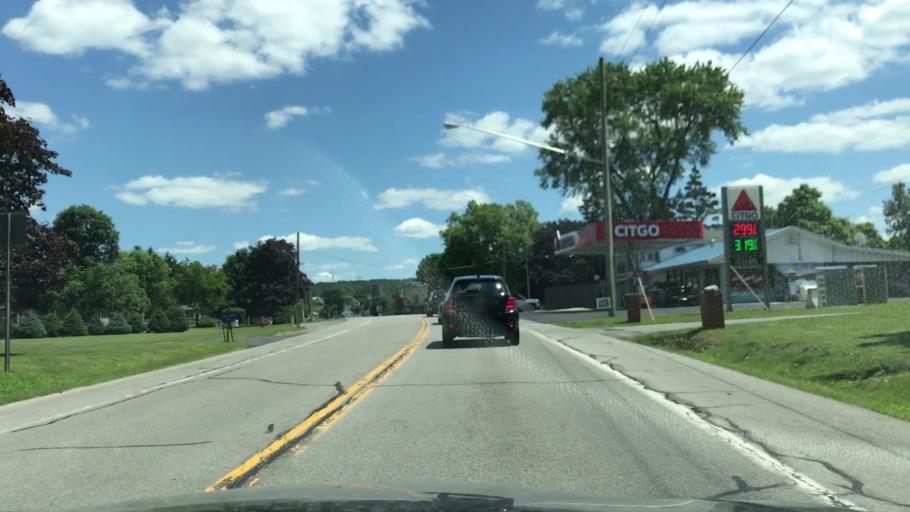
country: US
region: New York
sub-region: Wyoming County
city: Attica
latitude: 42.7580
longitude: -78.3092
